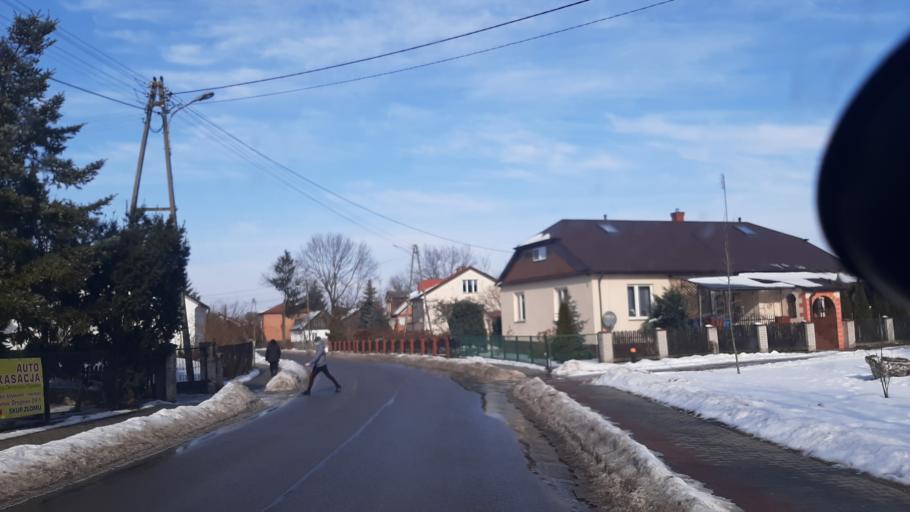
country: PL
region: Lublin Voivodeship
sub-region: Powiat pulawski
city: Baranow
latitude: 51.5587
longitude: 22.1355
